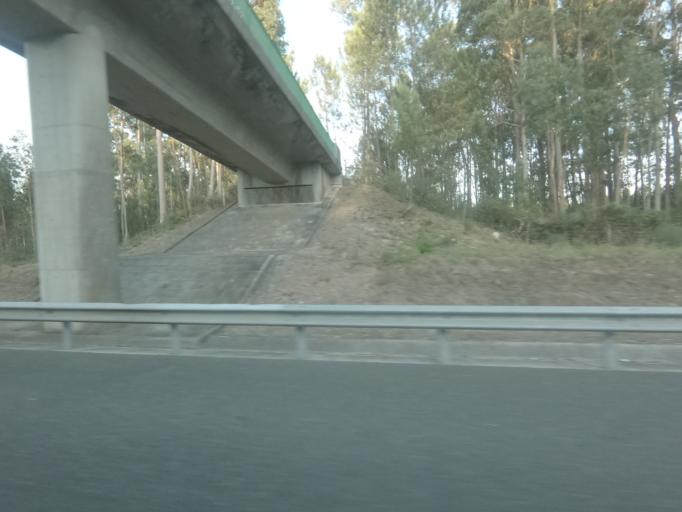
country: PT
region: Leiria
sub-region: Leiria
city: Santa Catarina da Serra
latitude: 39.6429
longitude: -8.6988
